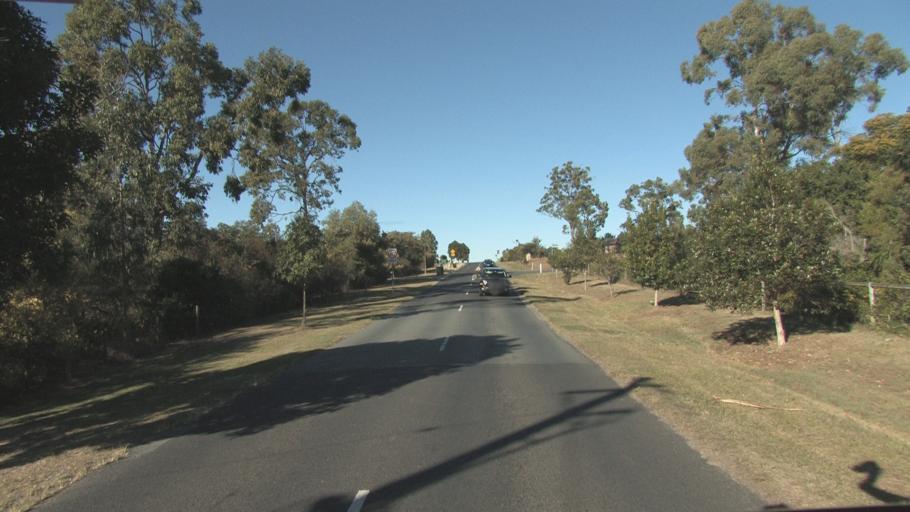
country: AU
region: Queensland
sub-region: Logan
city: North Maclean
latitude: -27.7438
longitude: 152.9677
